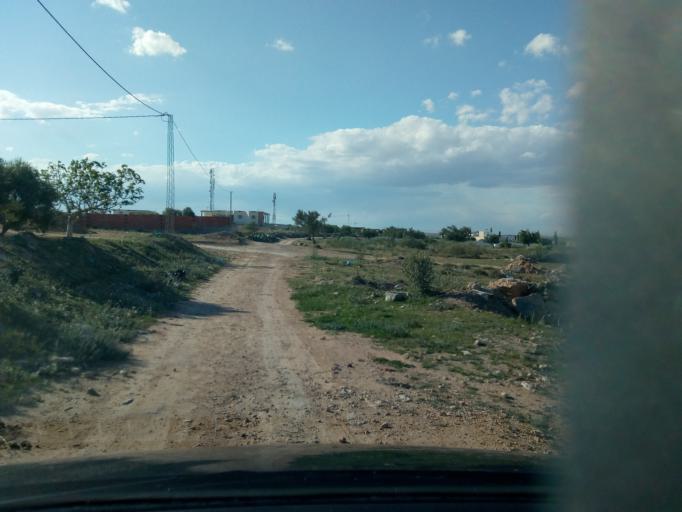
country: TN
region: Safaqis
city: Sfax
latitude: 34.7241
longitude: 10.6109
